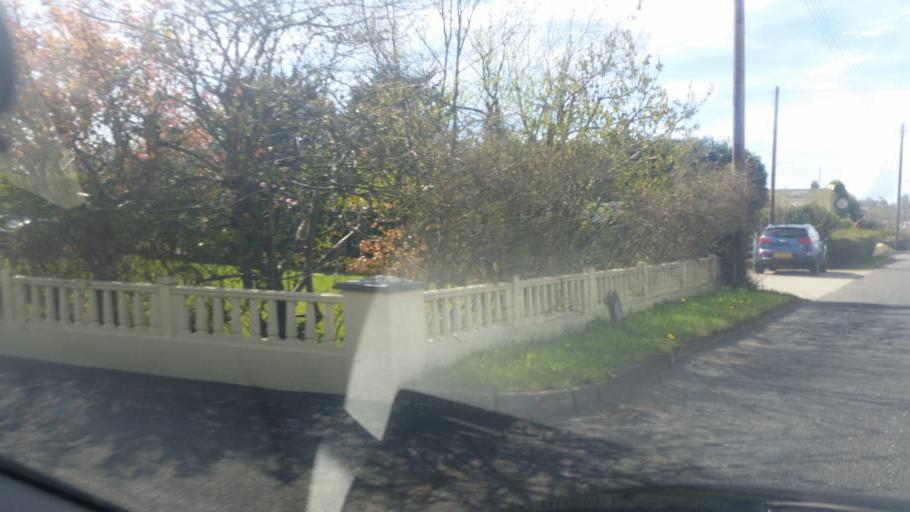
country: IE
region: Ulster
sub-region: County Donegal
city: Ballyshannon
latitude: 54.4755
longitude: -8.0927
